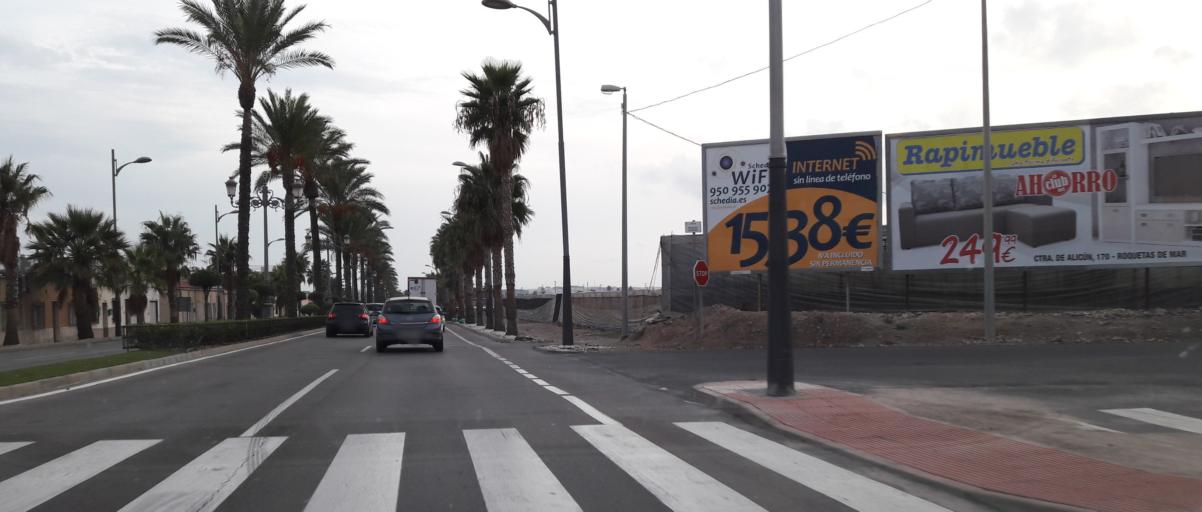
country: ES
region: Andalusia
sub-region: Provincia de Almeria
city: Roquetas de Mar
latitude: 36.7946
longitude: -2.6035
